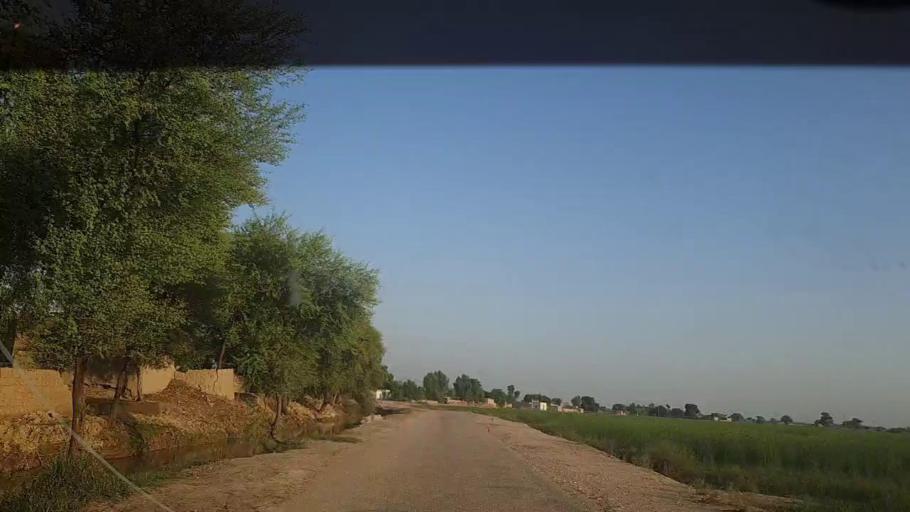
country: PK
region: Sindh
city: Thul
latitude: 28.1170
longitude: 68.8972
